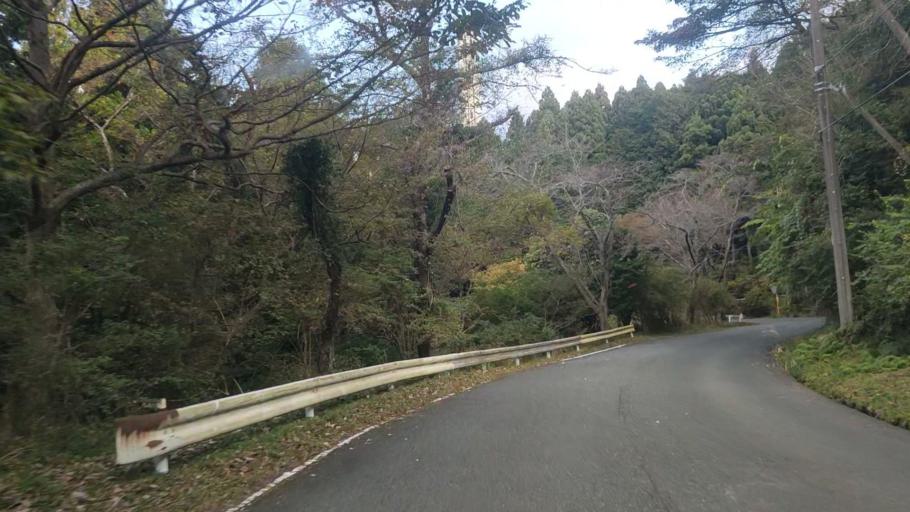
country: JP
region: Shizuoka
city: Ito
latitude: 34.9511
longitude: 139.0607
